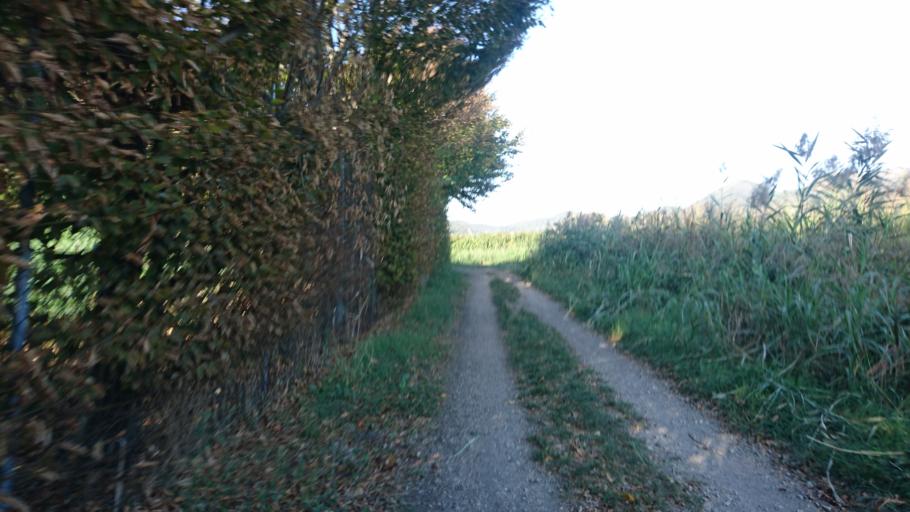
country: IT
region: Veneto
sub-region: Provincia di Padova
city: Galzignano
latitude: 45.2934
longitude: 11.7479
